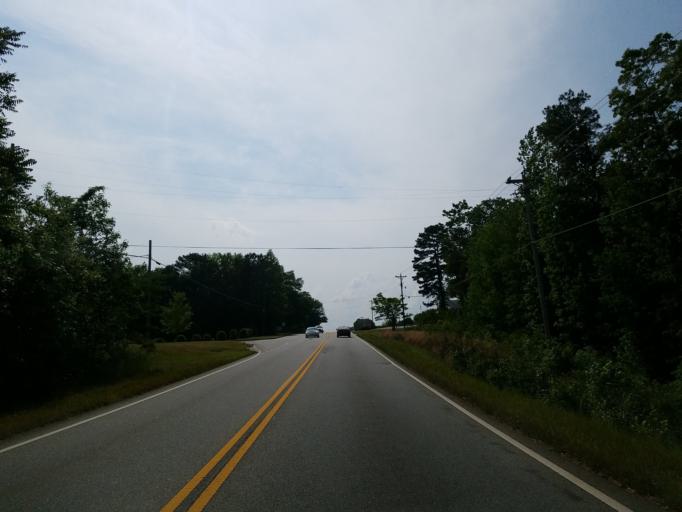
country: US
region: Georgia
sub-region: Paulding County
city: Hiram
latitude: 33.9101
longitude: -84.7872
